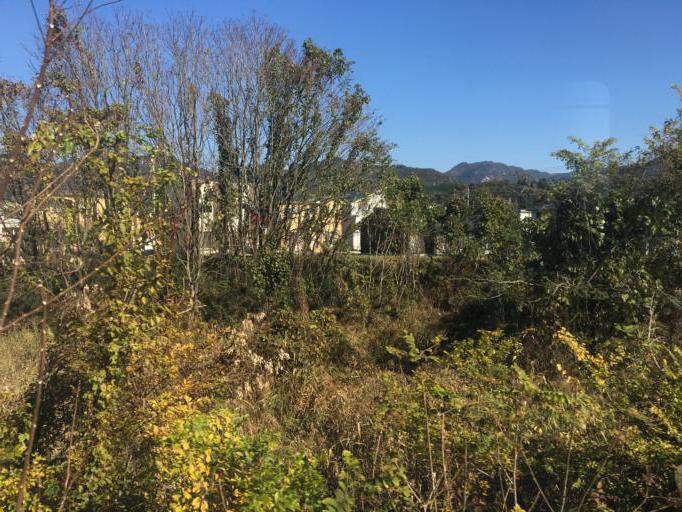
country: JP
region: Gunma
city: Kiryu
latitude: 36.3815
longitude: 139.3638
